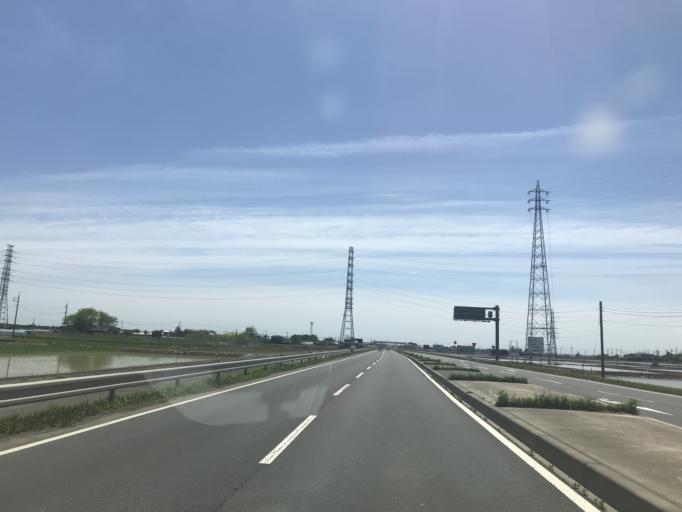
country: JP
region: Ibaraki
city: Ishige
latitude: 36.1785
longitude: 139.9907
